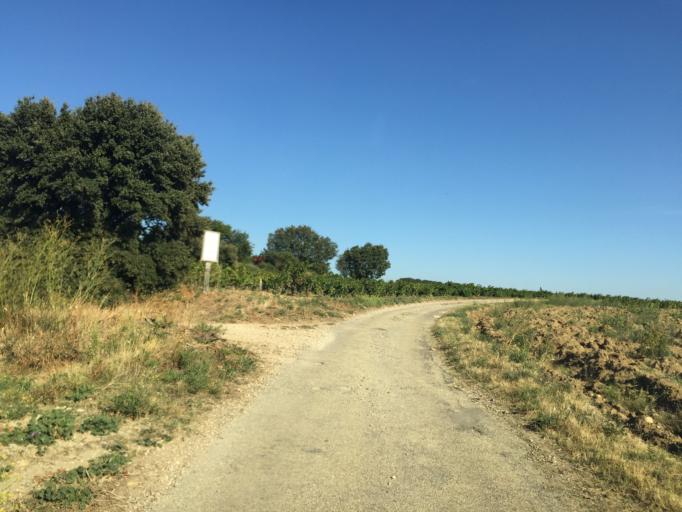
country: FR
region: Provence-Alpes-Cote d'Azur
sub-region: Departement du Vaucluse
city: Chateauneuf-du-Pape
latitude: 44.0582
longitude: 4.8485
